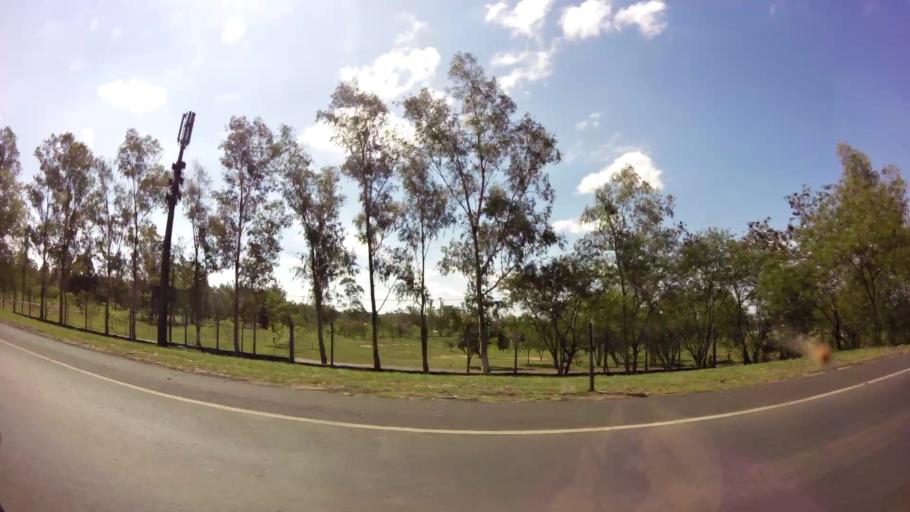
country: PY
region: Central
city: Fernando de la Mora
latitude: -25.2623
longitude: -57.5325
